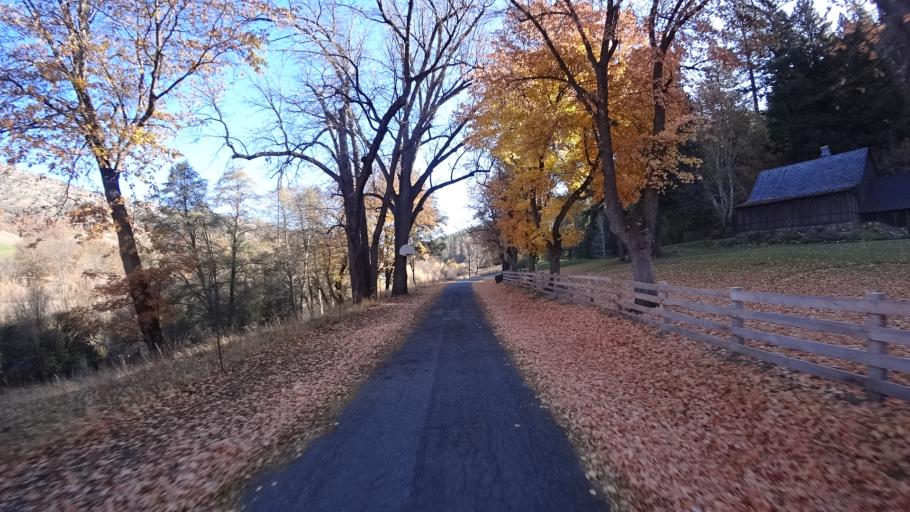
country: US
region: California
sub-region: Siskiyou County
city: Yreka
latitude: 41.8373
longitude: -122.9383
